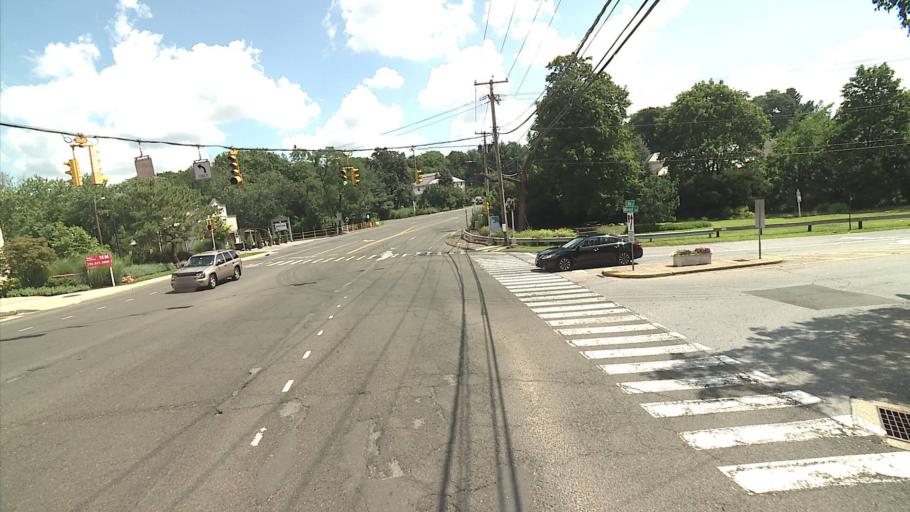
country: US
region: Connecticut
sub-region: Fairfield County
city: Stamford
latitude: 41.0606
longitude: -73.5082
